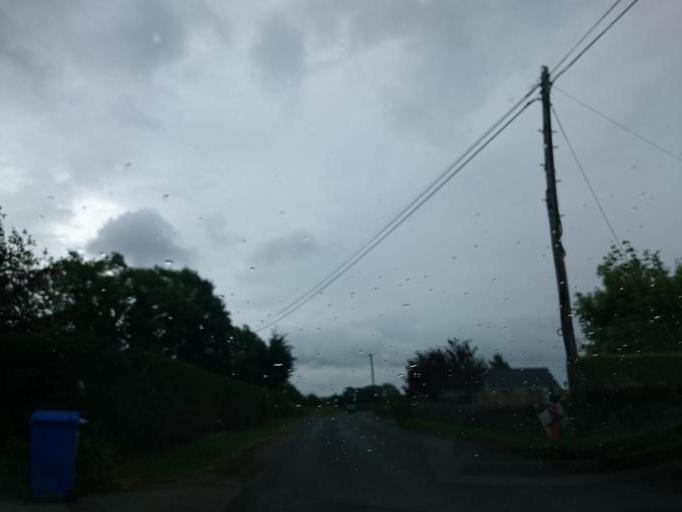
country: IE
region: Leinster
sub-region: Wicklow
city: Baltinglass
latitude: 52.9281
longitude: -6.6757
